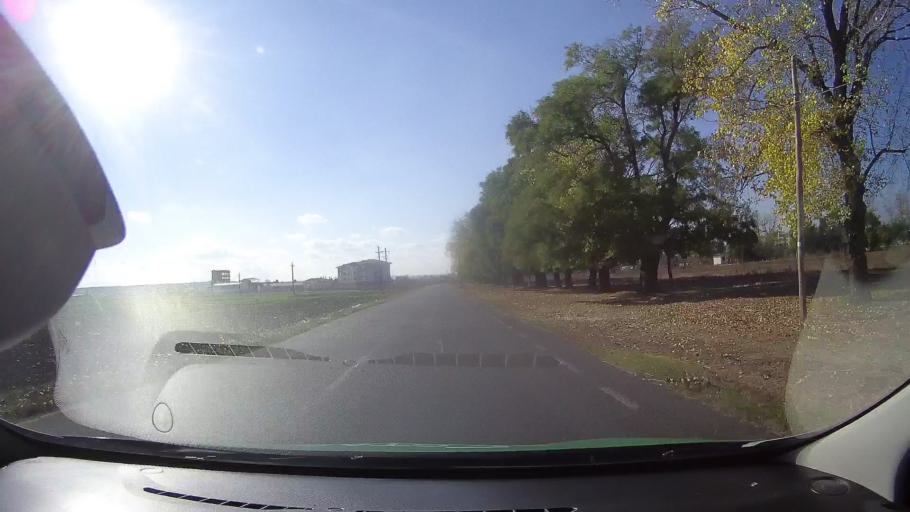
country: RO
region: Tulcea
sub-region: Comuna Baia
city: Baia
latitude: 44.7346
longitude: 28.6862
